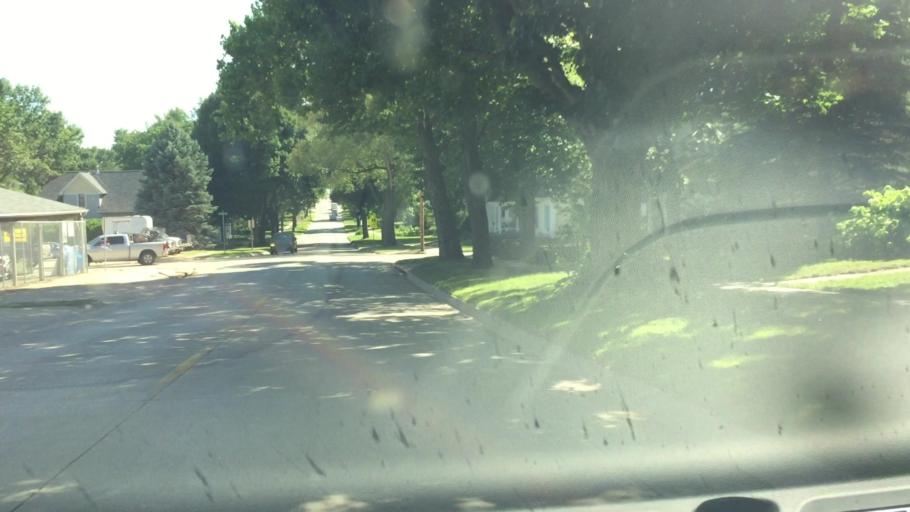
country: US
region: Iowa
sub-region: Linn County
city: Mount Vernon
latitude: 41.9211
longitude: -91.4182
